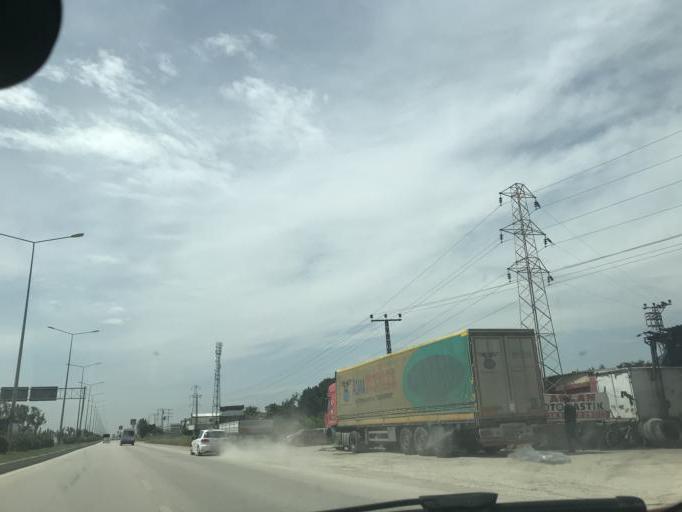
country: TR
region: Adana
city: Yuregir
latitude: 36.9823
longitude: 35.4269
